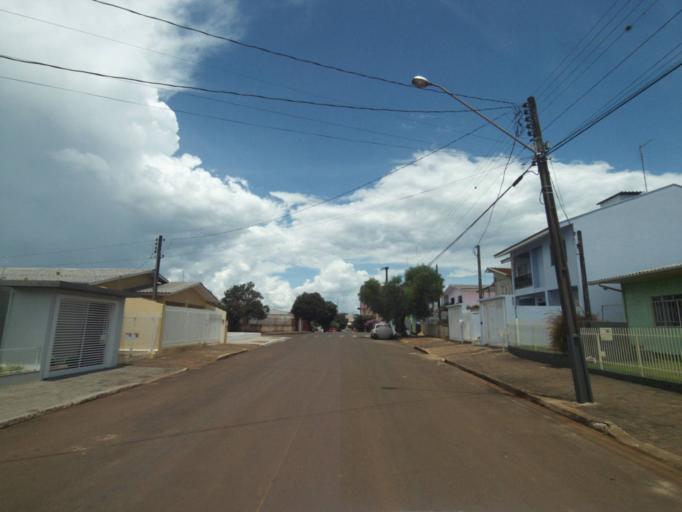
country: BR
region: Parana
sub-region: Guaraniacu
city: Guaraniacu
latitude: -25.0971
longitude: -52.8707
